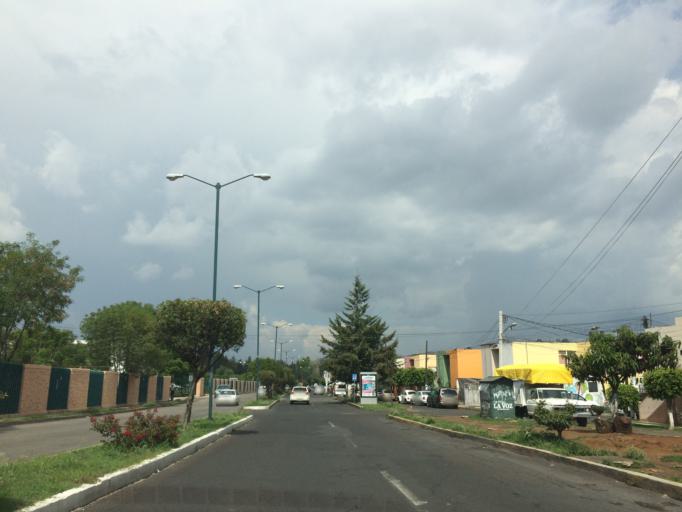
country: MX
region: Michoacan
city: Morelia
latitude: 19.6865
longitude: -101.2062
